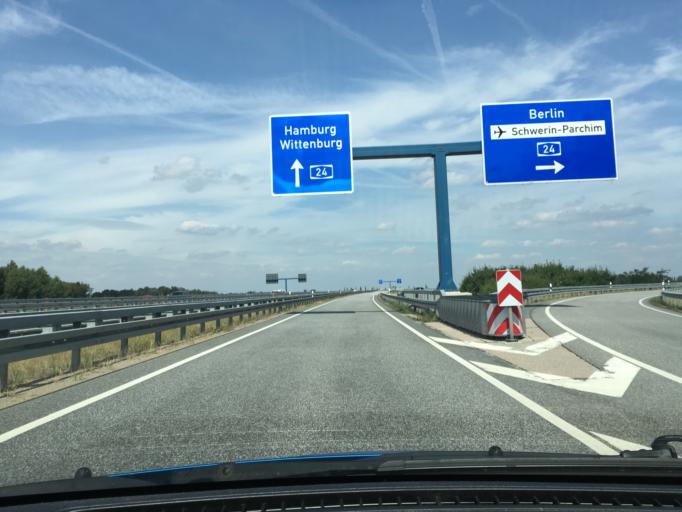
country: DE
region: Mecklenburg-Vorpommern
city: Gross Laasch
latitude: 53.4199
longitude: 11.5215
